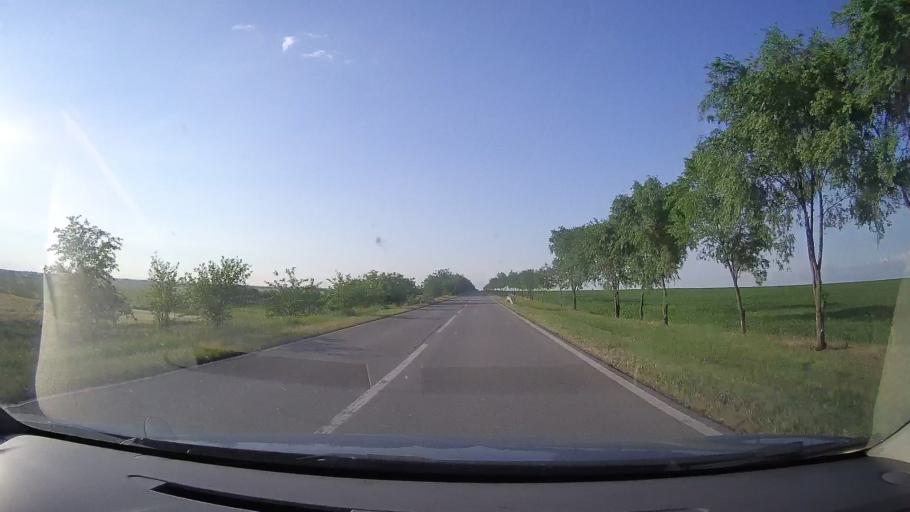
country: RO
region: Timis
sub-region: Comuna Moravita
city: Moravita
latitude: 45.1997
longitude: 21.2999
